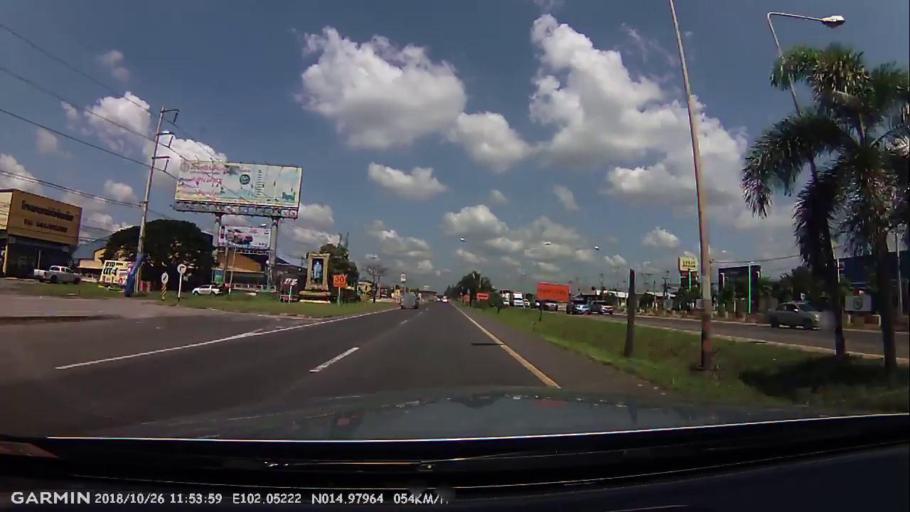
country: TH
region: Nakhon Ratchasima
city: Nakhon Ratchasima
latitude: 14.9797
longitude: 102.0522
